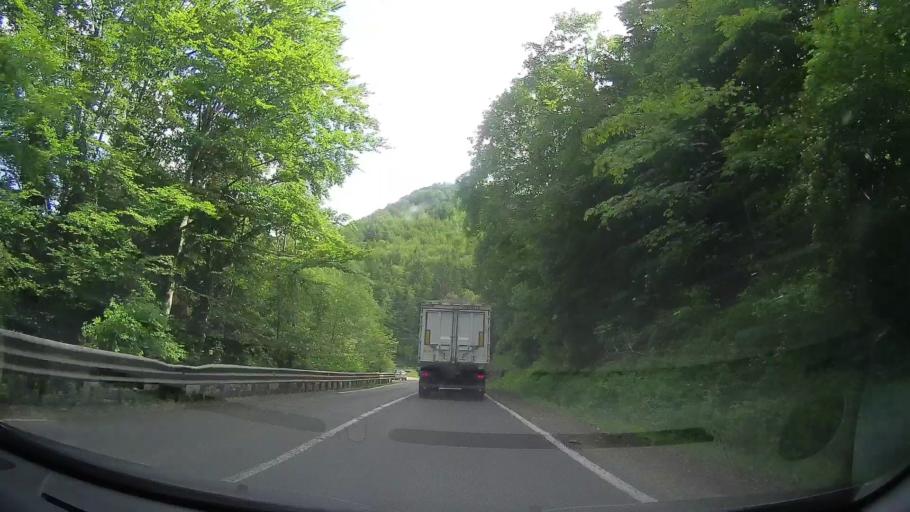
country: RO
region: Prahova
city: Maneciu
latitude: 45.3462
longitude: 25.9479
